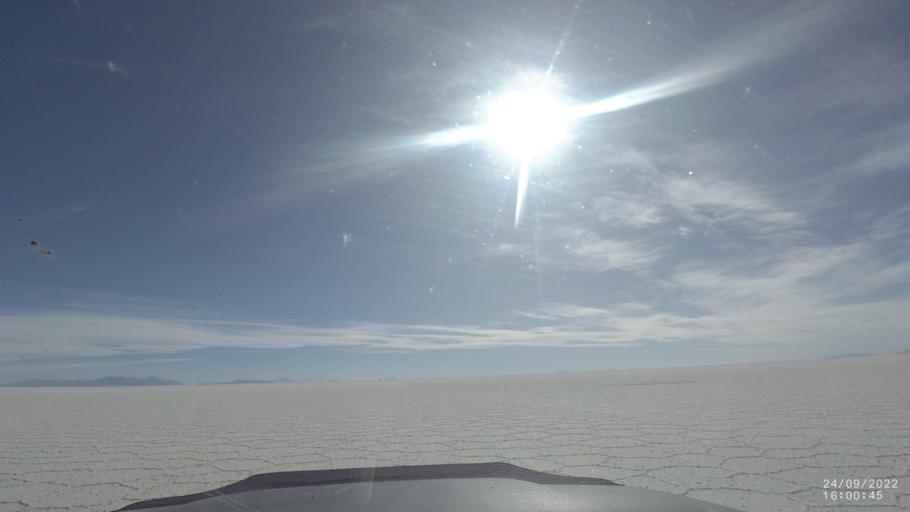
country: BO
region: Potosi
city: Colchani
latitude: -20.3222
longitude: -67.2520
